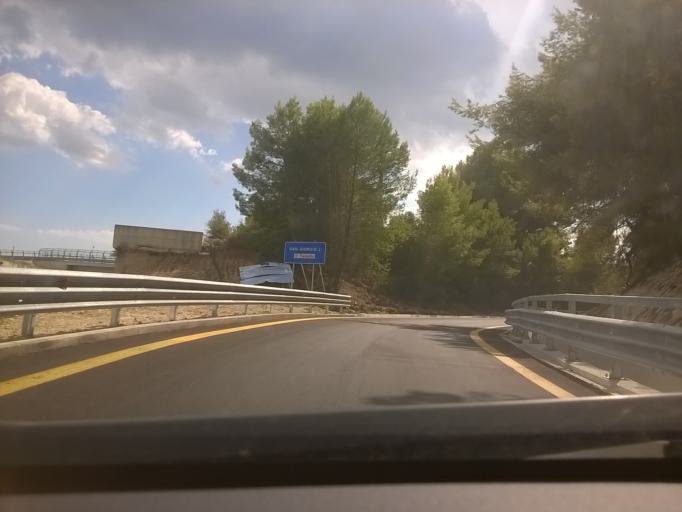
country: IT
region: Apulia
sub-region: Provincia di Taranto
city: Taranto
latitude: 40.4636
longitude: 17.2893
